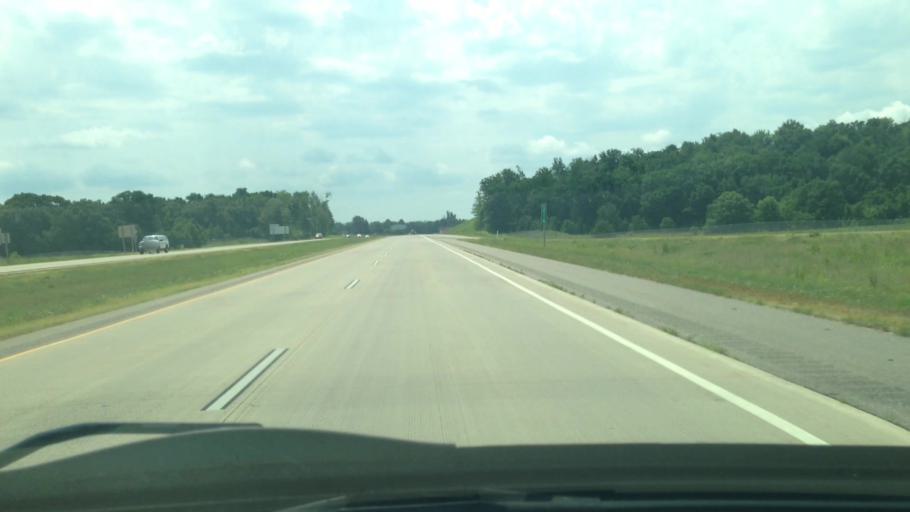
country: US
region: Wisconsin
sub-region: Sauk County
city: West Baraboo
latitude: 43.5131
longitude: -89.7838
